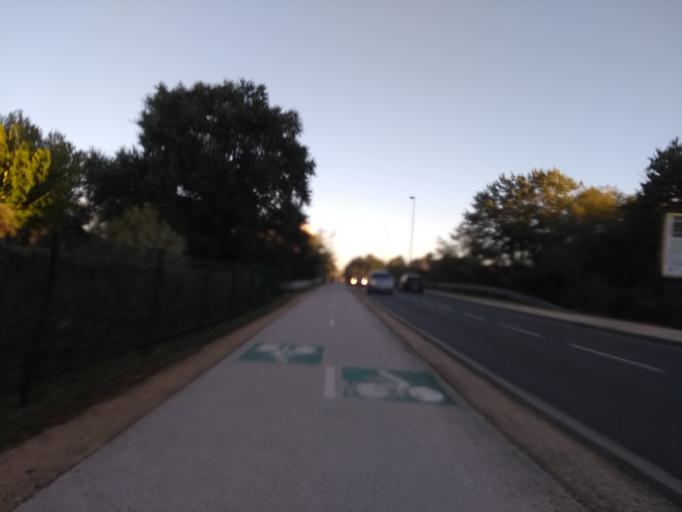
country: FR
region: Aquitaine
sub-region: Departement de la Gironde
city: Gradignan
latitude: 44.7892
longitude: -0.6125
